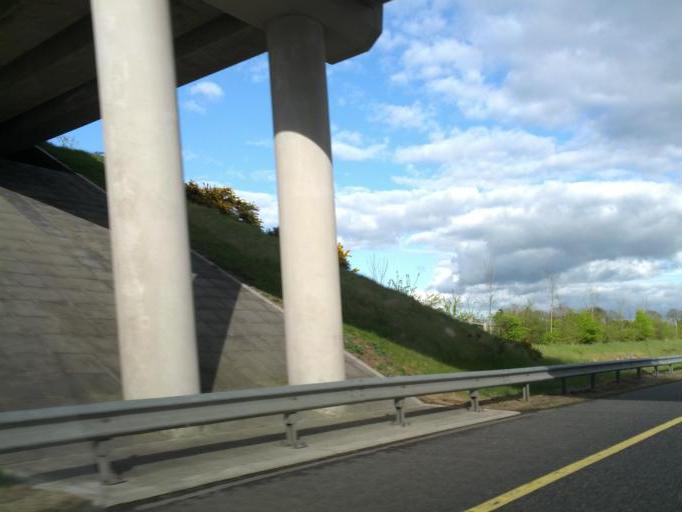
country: IE
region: Leinster
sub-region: Uibh Fhaili
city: Clara
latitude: 53.3879
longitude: -7.6037
